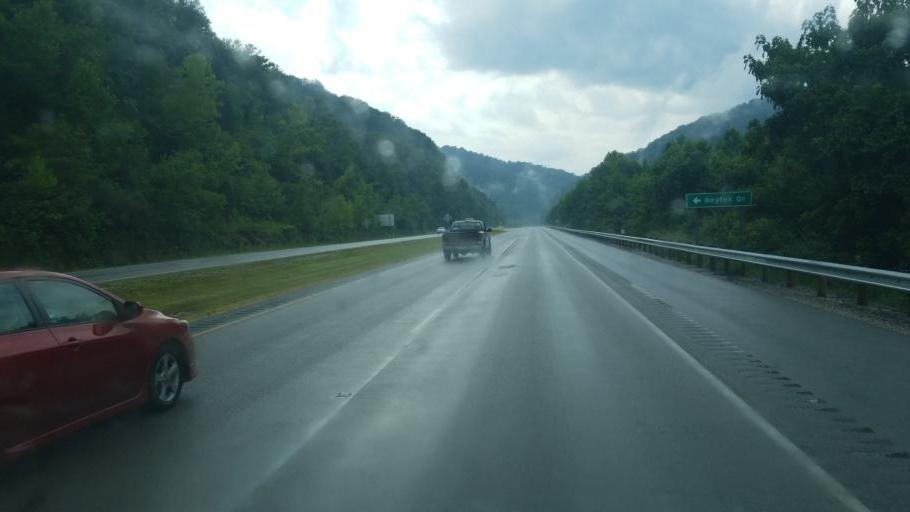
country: US
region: West Virginia
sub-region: Logan County
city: Chapmanville
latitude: 37.9868
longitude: -81.9442
